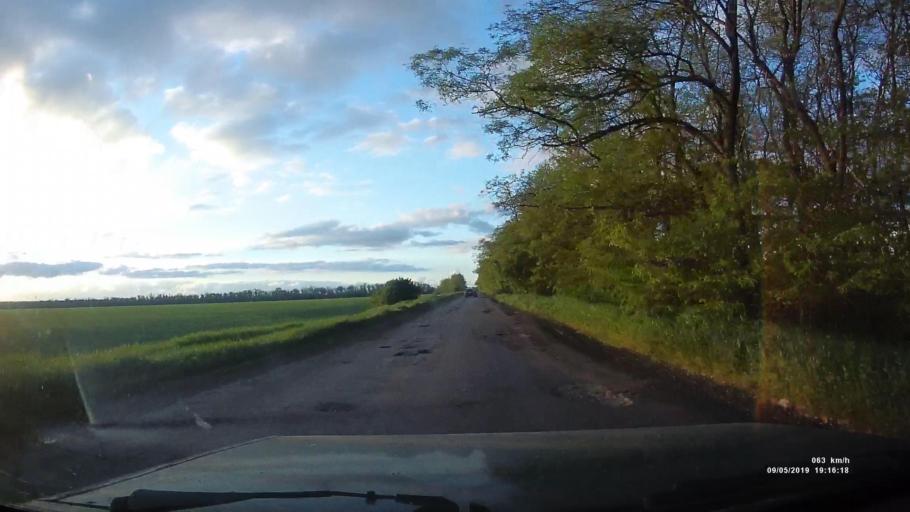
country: RU
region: Krasnodarskiy
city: Kanelovskaya
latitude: 46.7767
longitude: 39.2115
